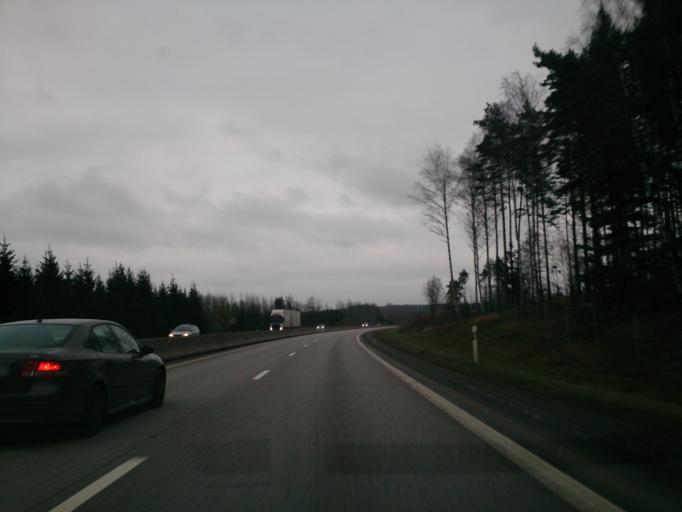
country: SE
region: OEstergoetland
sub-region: Norrkopings Kommun
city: Kimstad
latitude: 58.5207
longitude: 16.0023
